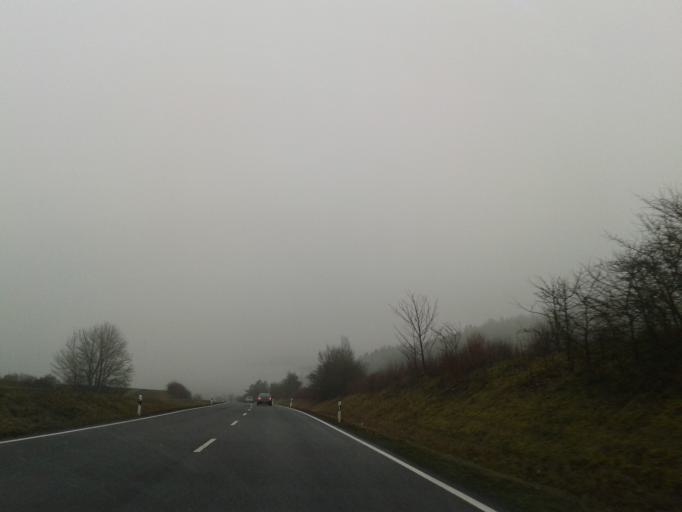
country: DE
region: Bavaria
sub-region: Regierungsbezirk Unterfranken
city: Hofheim in Unterfranken
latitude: 50.1245
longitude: 10.5640
